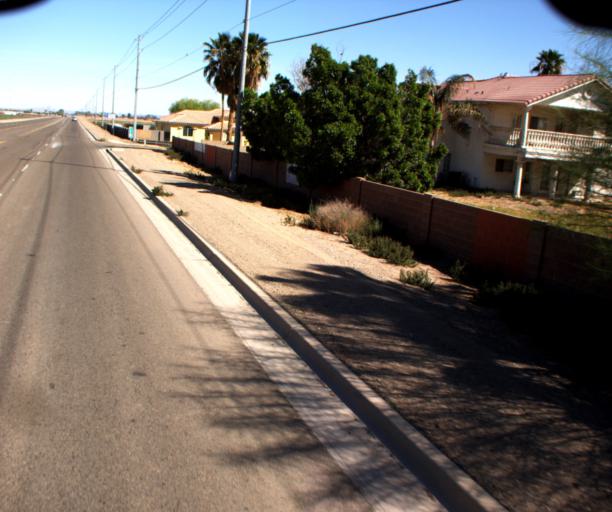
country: US
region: Arizona
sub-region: Yuma County
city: Somerton
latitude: 32.6424
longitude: -114.6500
